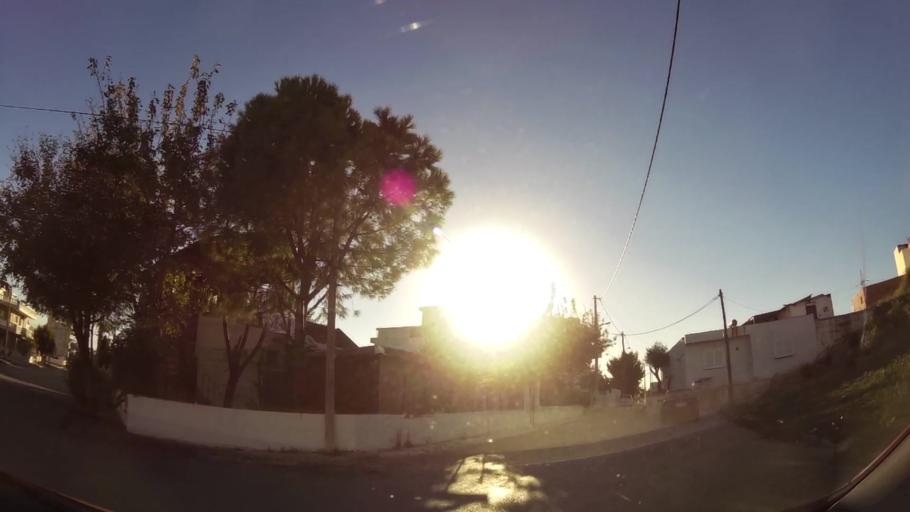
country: GR
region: Attica
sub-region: Nomarchia Anatolikis Attikis
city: Acharnes
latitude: 38.0760
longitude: 23.7261
